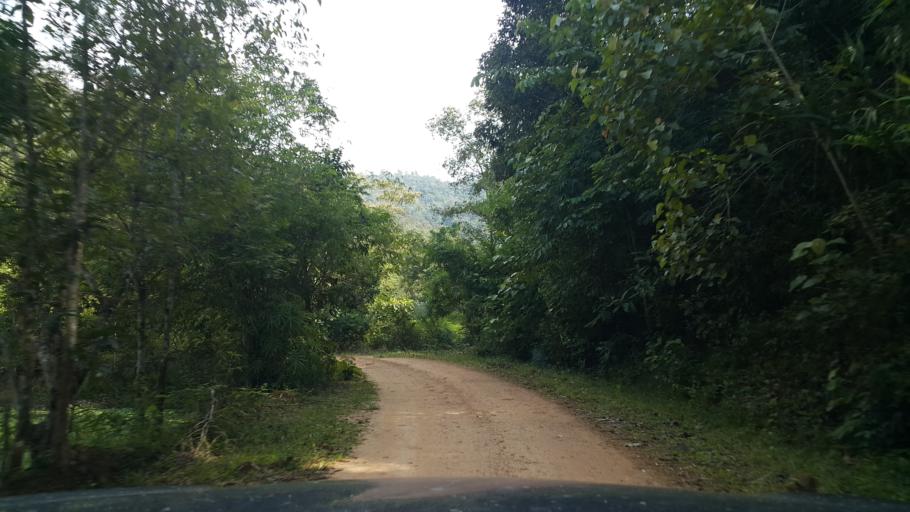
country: TH
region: Chiang Mai
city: Phrao
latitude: 19.0788
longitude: 99.2502
